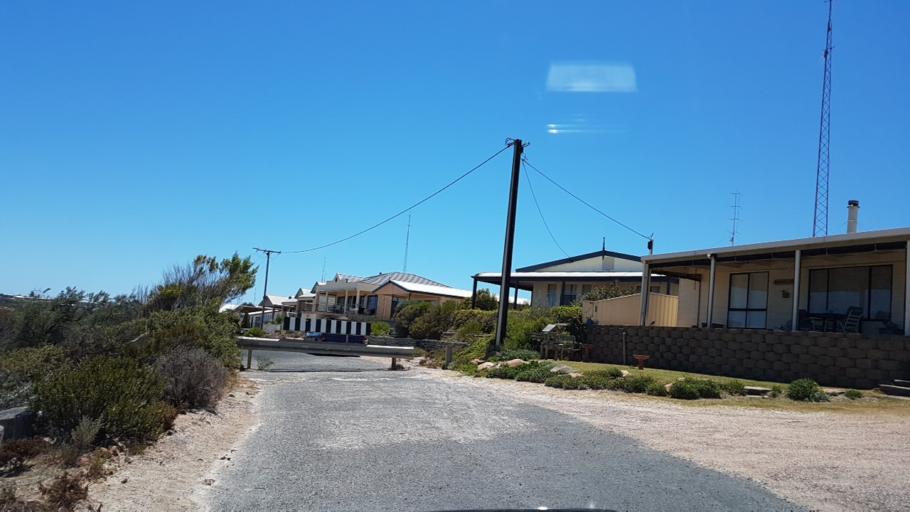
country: AU
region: South Australia
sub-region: Copper Coast
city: Wallaroo
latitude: -33.9064
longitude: 137.6312
